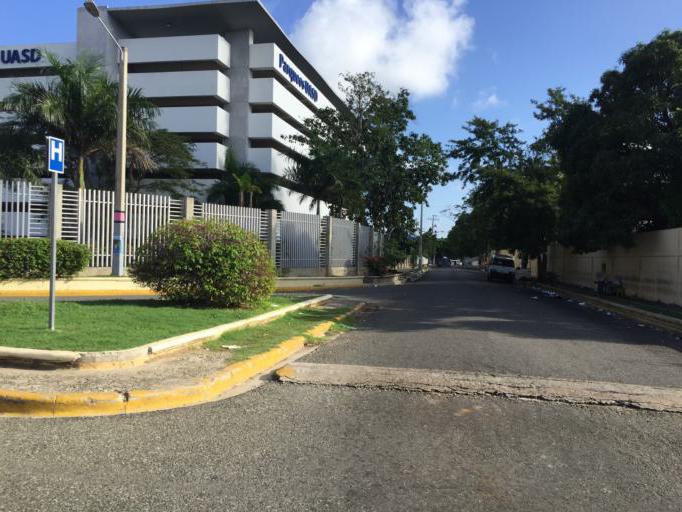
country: DO
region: Nacional
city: La Julia
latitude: 18.4590
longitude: -69.9215
